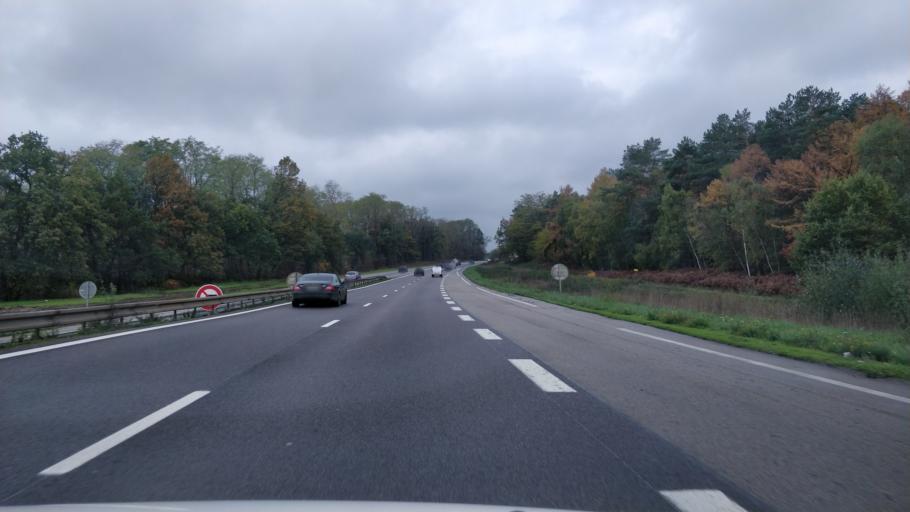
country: FR
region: Haute-Normandie
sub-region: Departement de la Seine-Maritime
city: Le Grand-Quevilly
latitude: 49.3785
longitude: 1.0477
